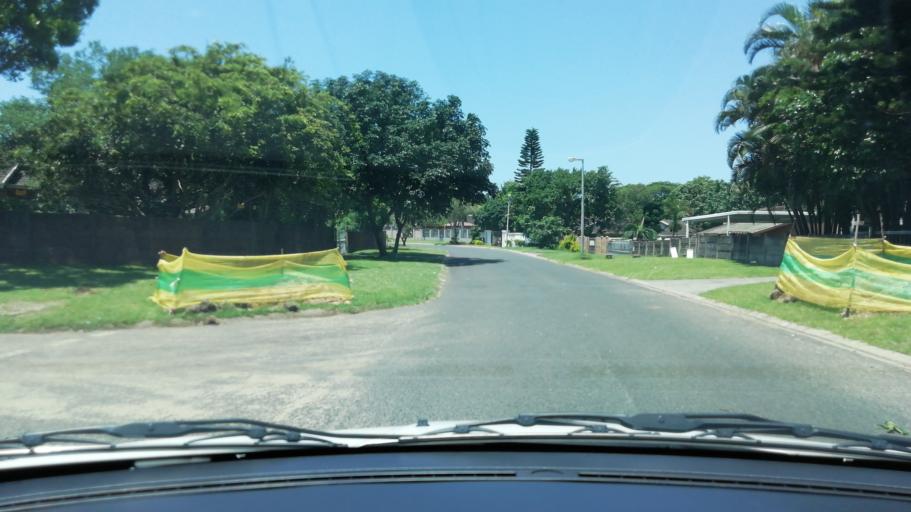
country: ZA
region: KwaZulu-Natal
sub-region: uThungulu District Municipality
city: Richards Bay
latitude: -28.7353
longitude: 32.0618
